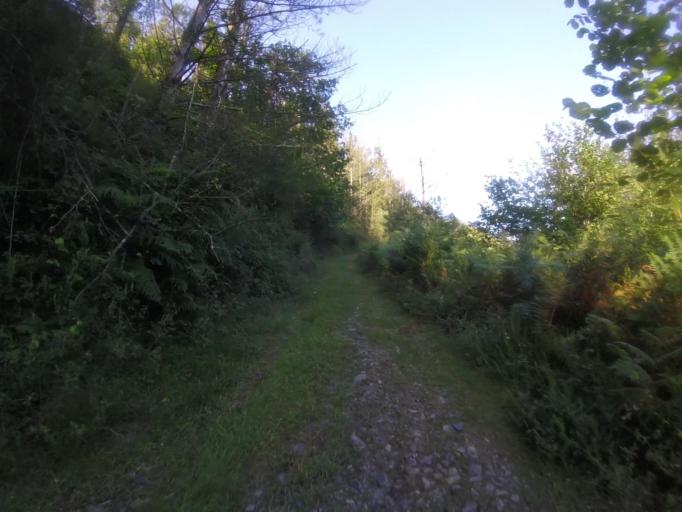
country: ES
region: Navarre
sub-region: Provincia de Navarra
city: Arano
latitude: 43.2300
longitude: -1.9087
